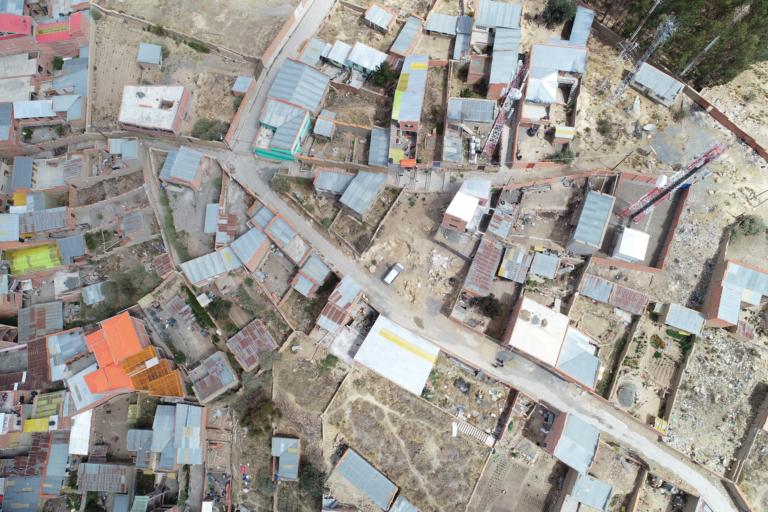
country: BO
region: La Paz
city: Achacachi
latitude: -16.0421
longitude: -68.6834
